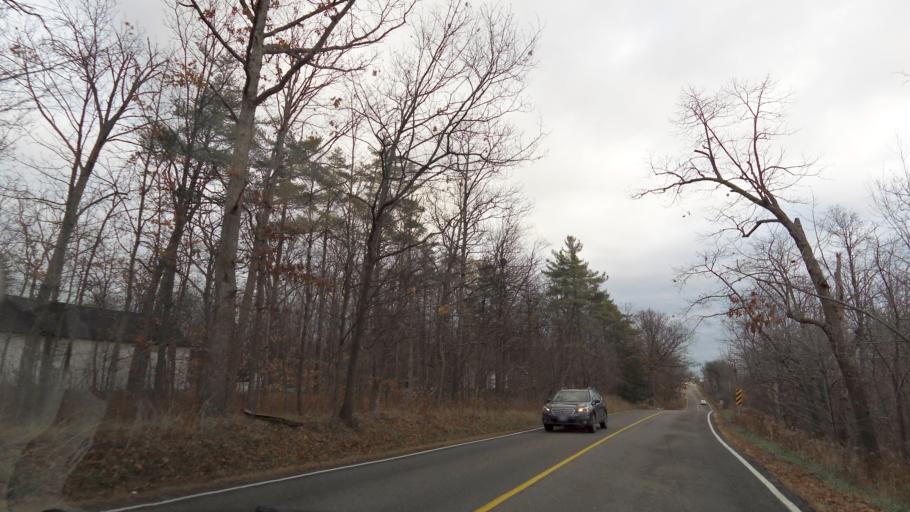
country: CA
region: Ontario
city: Burlington
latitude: 43.4038
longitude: -79.8396
